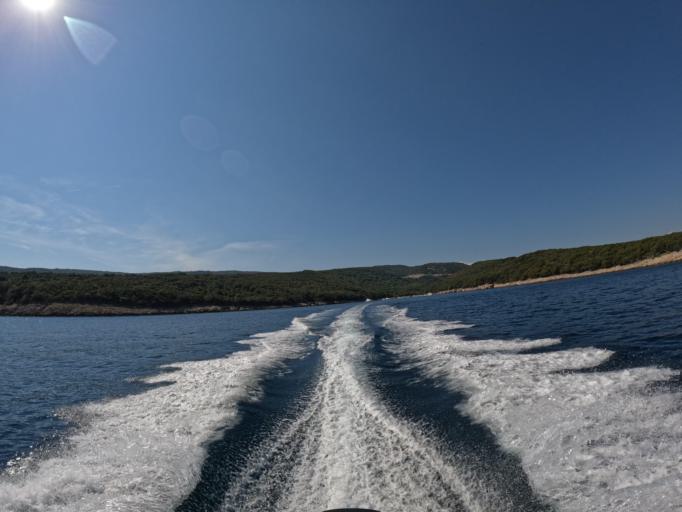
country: HR
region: Primorsko-Goranska
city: Cres
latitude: 44.9465
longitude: 14.4678
